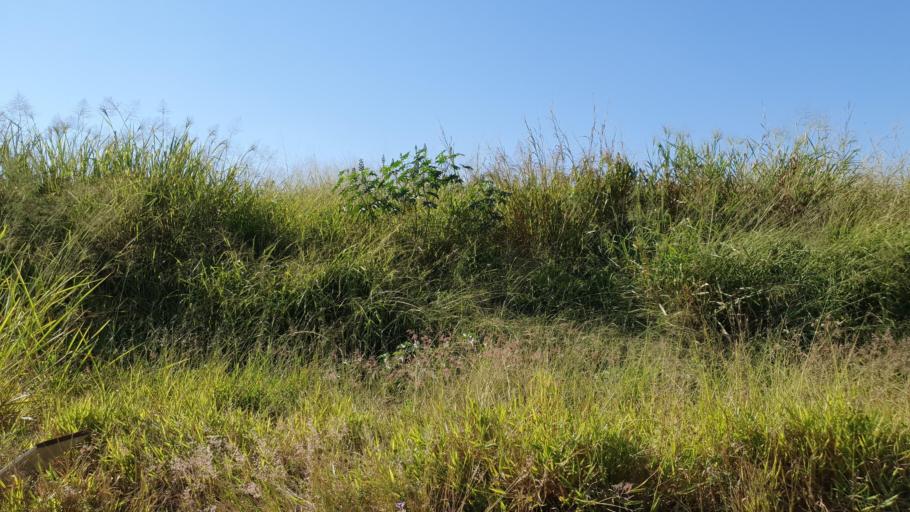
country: BR
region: Sao Paulo
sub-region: Sorocaba
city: Sorocaba
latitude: -23.4398
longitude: -47.4397
